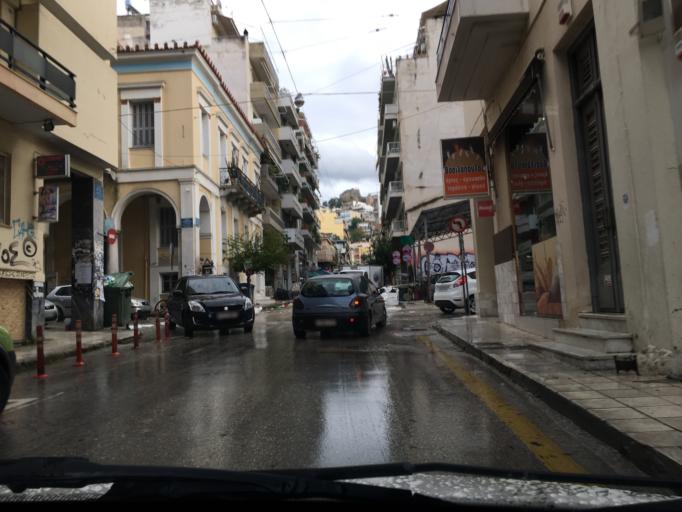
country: GR
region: West Greece
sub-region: Nomos Achaias
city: Patra
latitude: 38.2483
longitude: 21.7394
